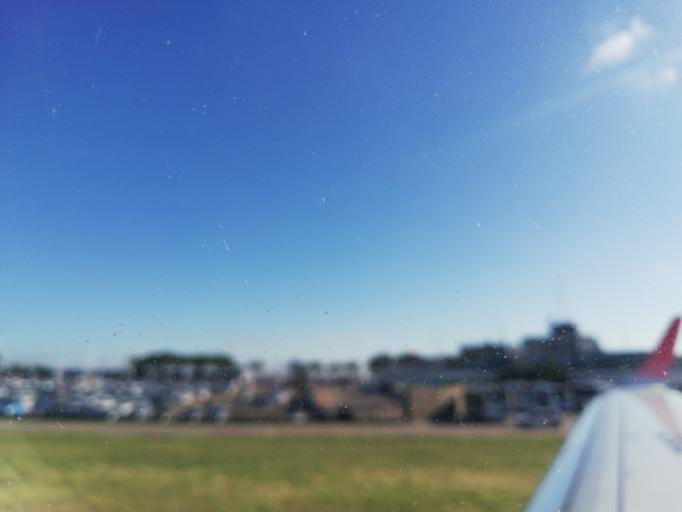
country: AR
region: Buenos Aires F.D.
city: Colegiales
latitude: -34.5574
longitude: -58.4174
